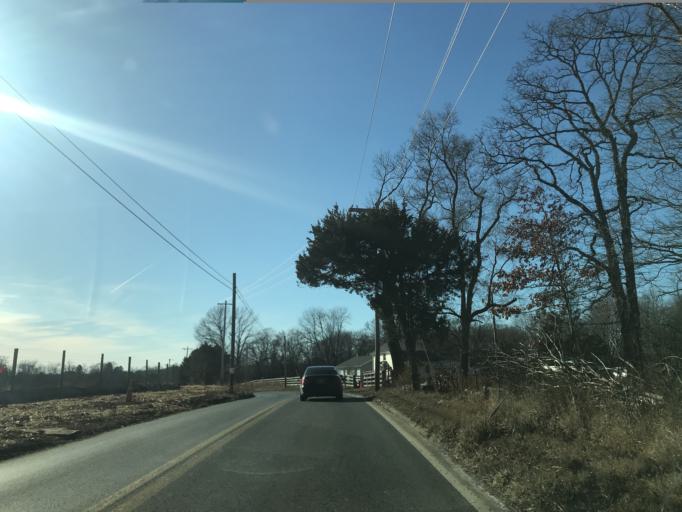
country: US
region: Maryland
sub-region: Charles County
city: Waldorf
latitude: 38.6740
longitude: -76.9696
